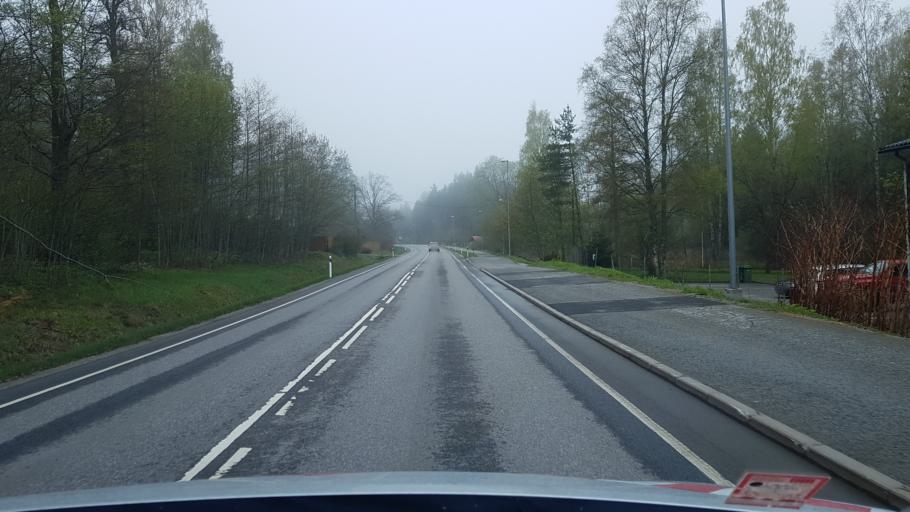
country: EE
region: Harju
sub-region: Viimsi vald
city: Viimsi
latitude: 59.5307
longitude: 24.8749
